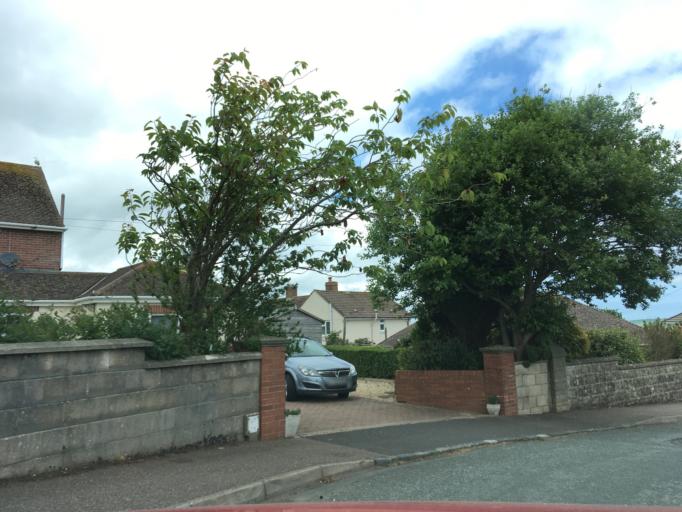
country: GB
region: England
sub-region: Devon
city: Dartmouth
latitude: 50.3492
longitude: -3.5990
